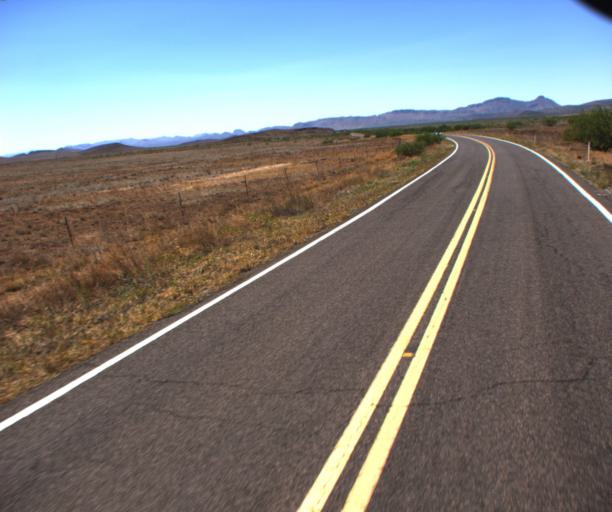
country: US
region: Arizona
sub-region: Cochise County
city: Douglas
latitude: 31.5470
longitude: -109.2809
